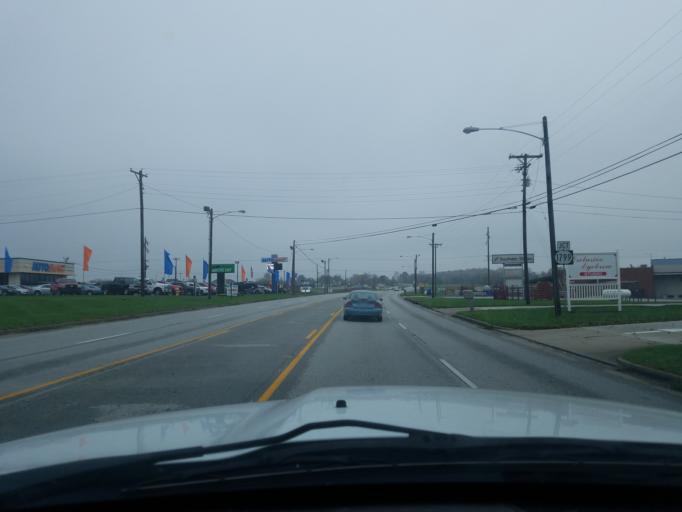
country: US
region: Kentucky
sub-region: Taylor County
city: Campbellsville
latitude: 37.3570
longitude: -85.3240
